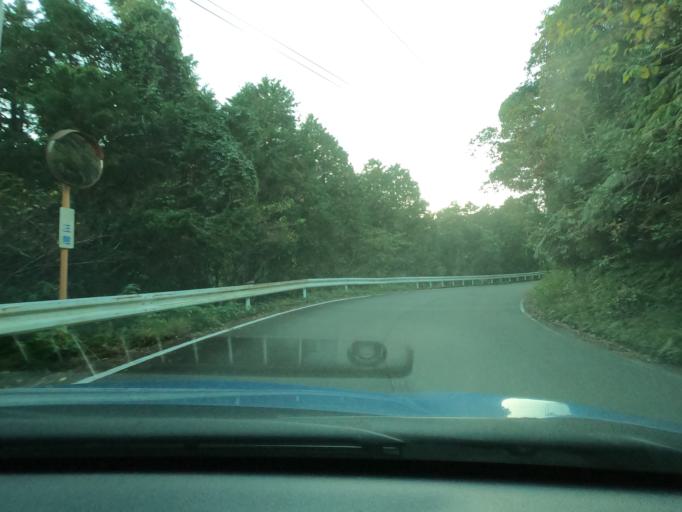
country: JP
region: Kagoshima
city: Satsumasendai
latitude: 31.8157
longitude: 130.4755
